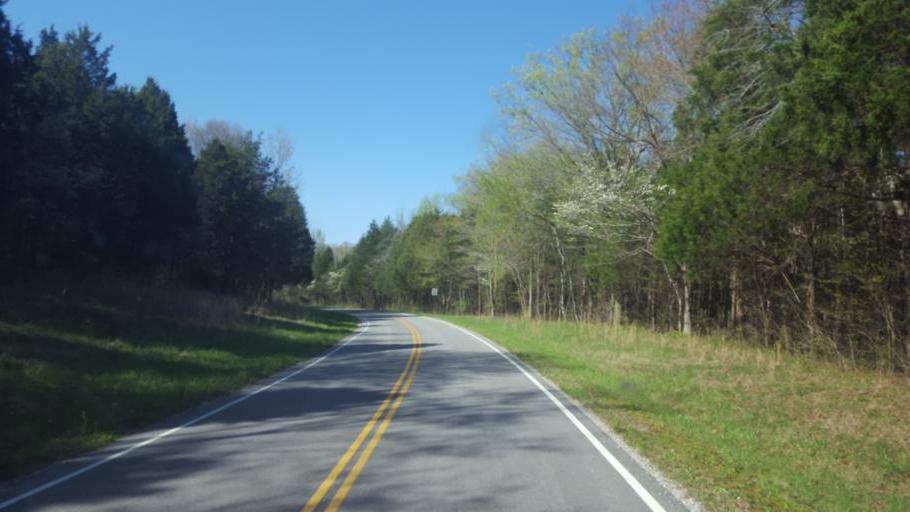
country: US
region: Kentucky
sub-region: Edmonson County
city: Brownsville
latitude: 37.1473
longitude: -86.1591
